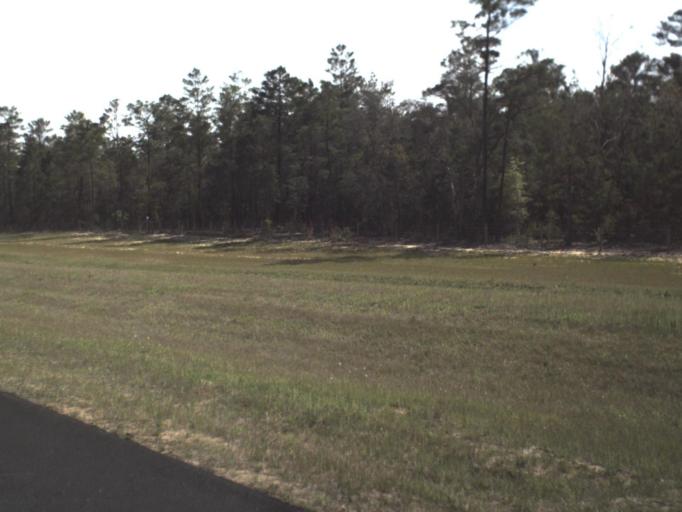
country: US
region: Florida
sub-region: Okaloosa County
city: Niceville
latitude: 30.5307
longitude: -86.4190
